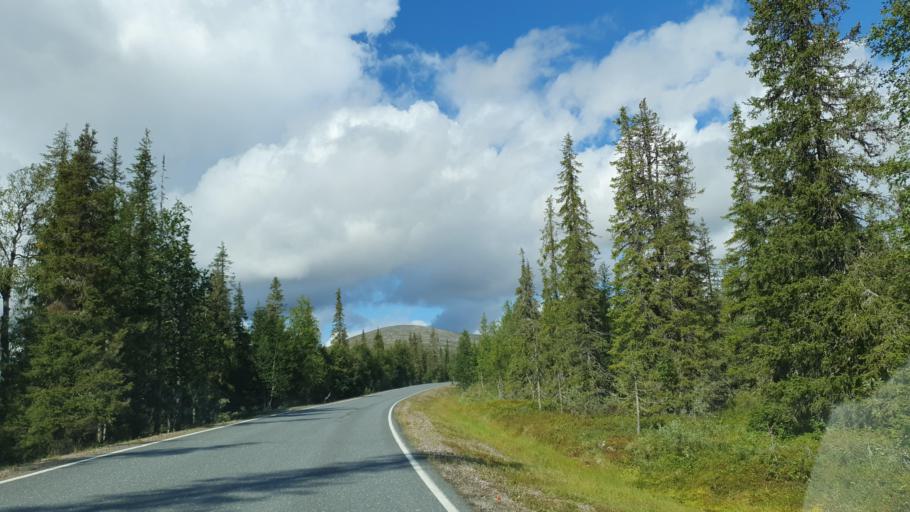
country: FI
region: Lapland
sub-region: Tunturi-Lappi
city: Muonio
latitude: 68.0348
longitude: 24.0677
